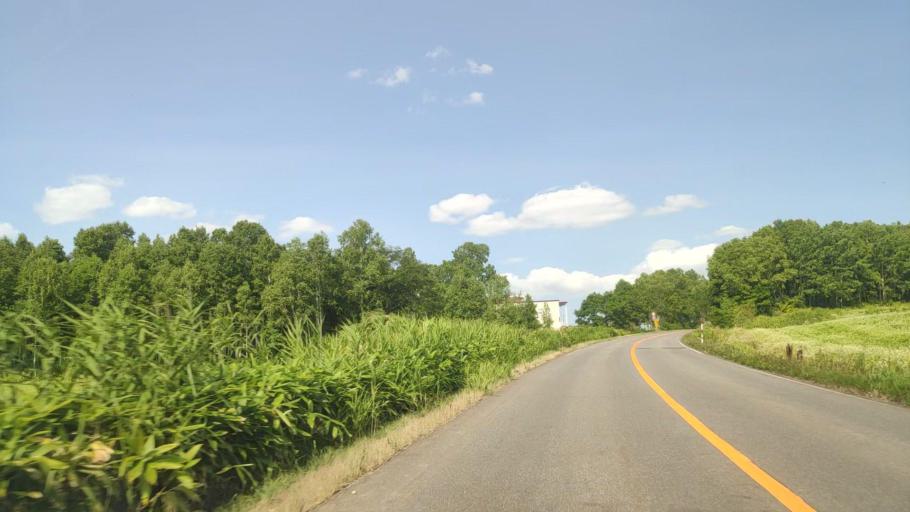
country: JP
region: Hokkaido
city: Nayoro
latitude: 44.2805
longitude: 142.4243
